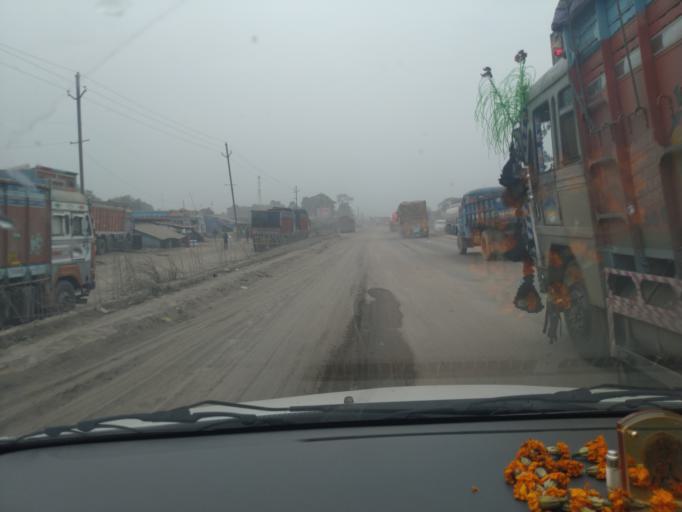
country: IN
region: Bihar
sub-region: Rohtas
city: Dehri
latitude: 24.9145
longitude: 84.1603
